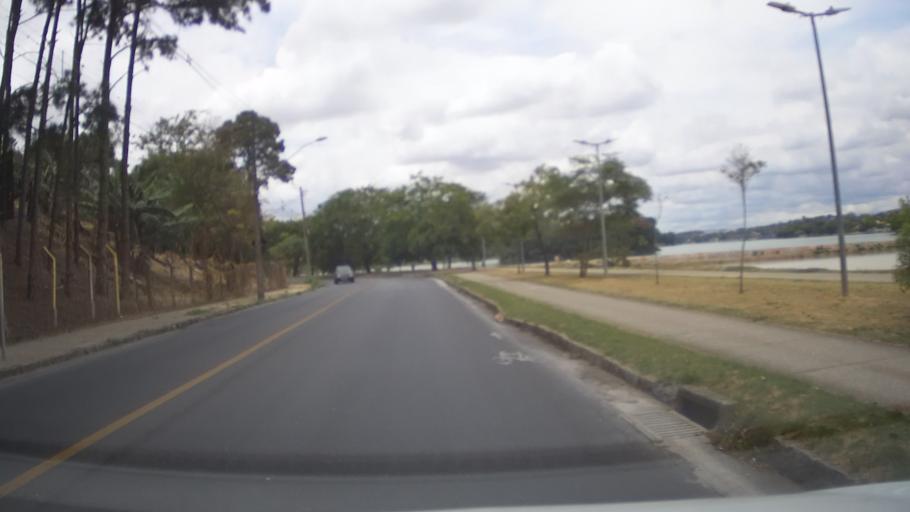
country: BR
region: Minas Gerais
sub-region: Belo Horizonte
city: Belo Horizonte
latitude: -19.8465
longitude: -43.9961
